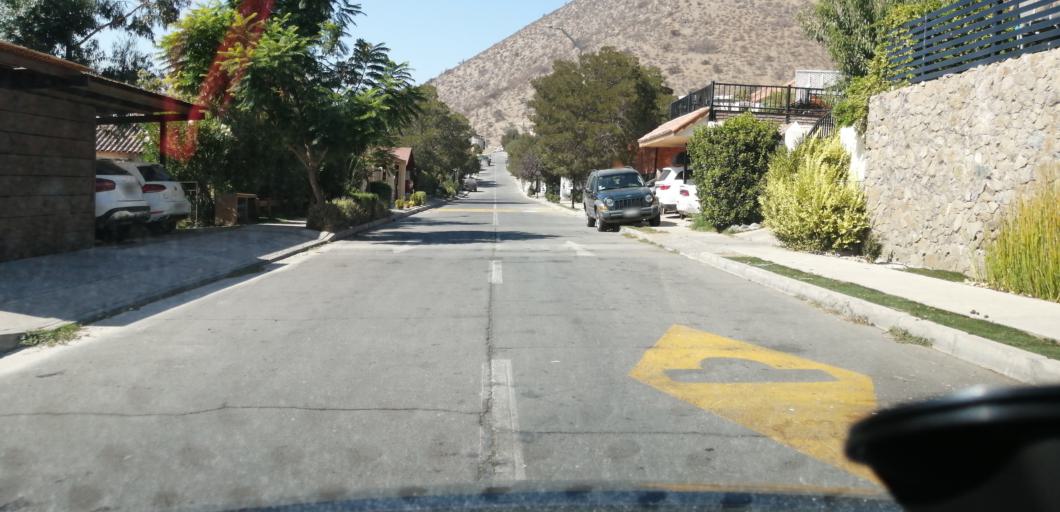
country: CL
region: Santiago Metropolitan
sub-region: Provincia de Santiago
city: Lo Prado
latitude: -33.4571
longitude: -70.8255
